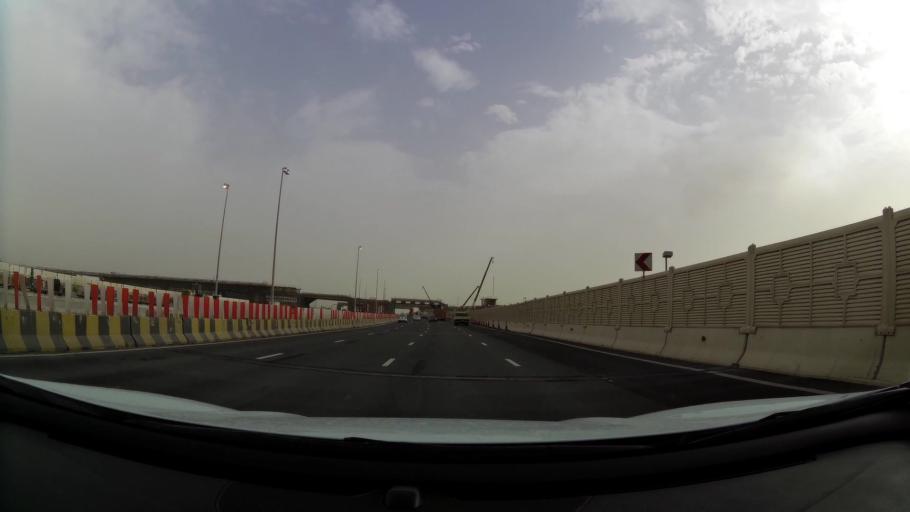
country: AE
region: Abu Dhabi
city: Abu Dhabi
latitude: 24.4541
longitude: 54.6237
